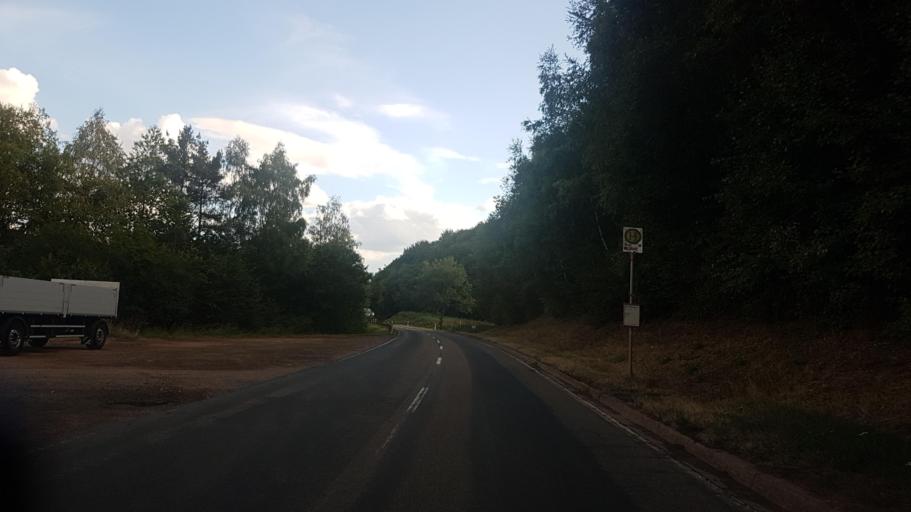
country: DE
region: Rheinland-Pfalz
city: Dienstweiler
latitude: 49.6324
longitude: 7.1935
